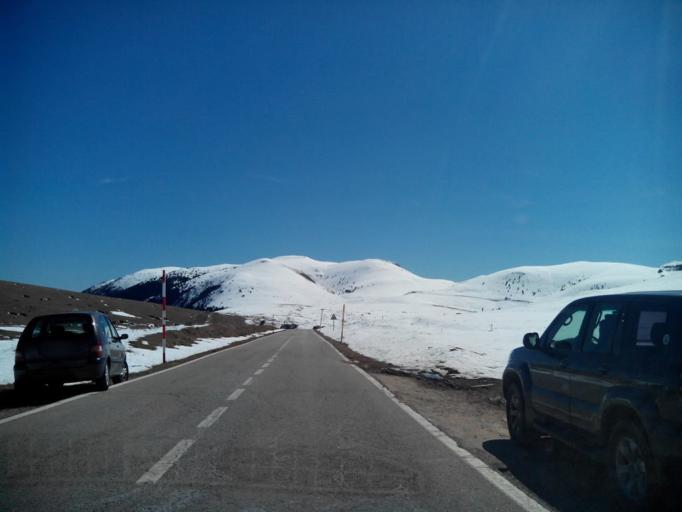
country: ES
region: Catalonia
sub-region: Provincia de Girona
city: Toses
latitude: 42.3211
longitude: 1.9646
